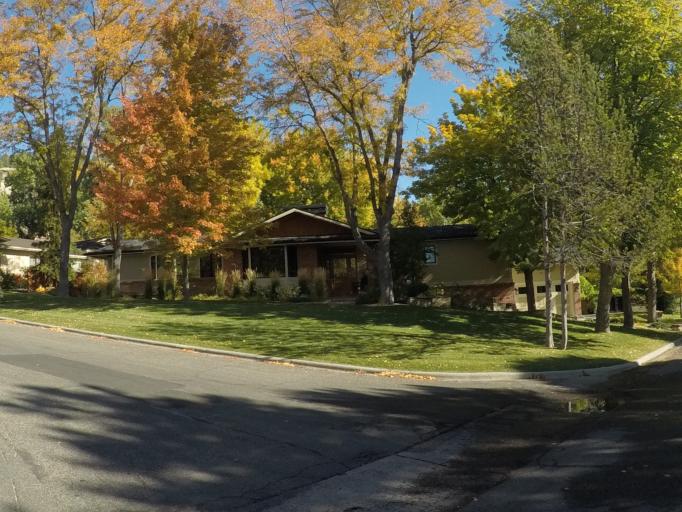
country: US
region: Montana
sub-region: Yellowstone County
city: Billings
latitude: 45.8002
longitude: -108.5862
